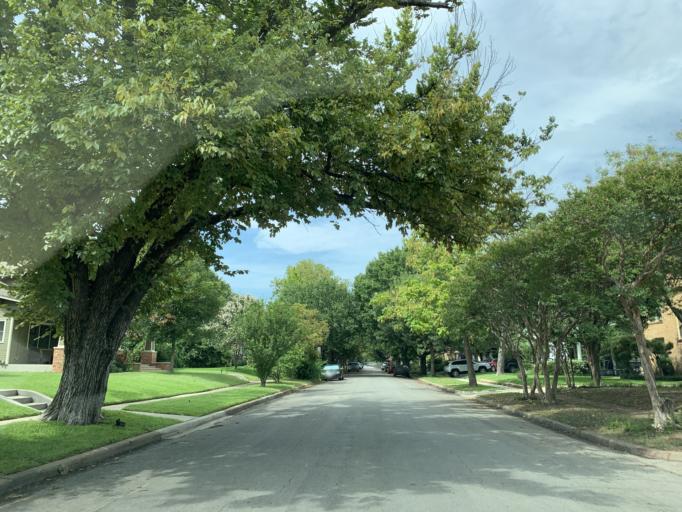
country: US
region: Texas
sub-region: Dallas County
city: Cockrell Hill
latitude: 32.7417
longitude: -96.8454
